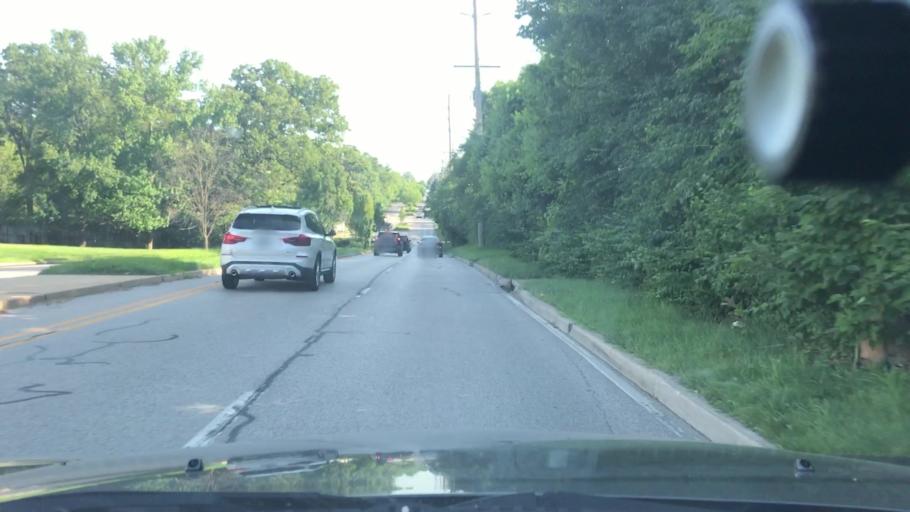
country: US
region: Missouri
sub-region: Saint Louis County
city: Creve Coeur
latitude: 38.6473
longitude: -90.4433
